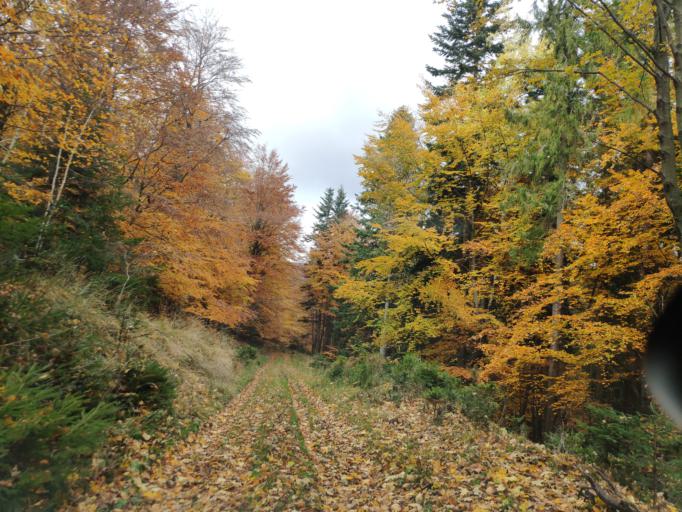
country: SK
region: Kosicky
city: Medzev
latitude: 48.7550
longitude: 20.9828
